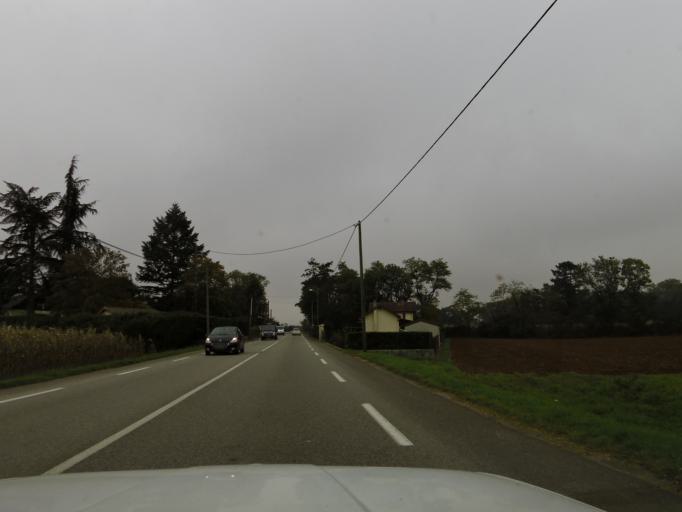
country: FR
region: Rhone-Alpes
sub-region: Departement de l'Ain
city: Meximieux
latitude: 45.8948
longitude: 5.1916
